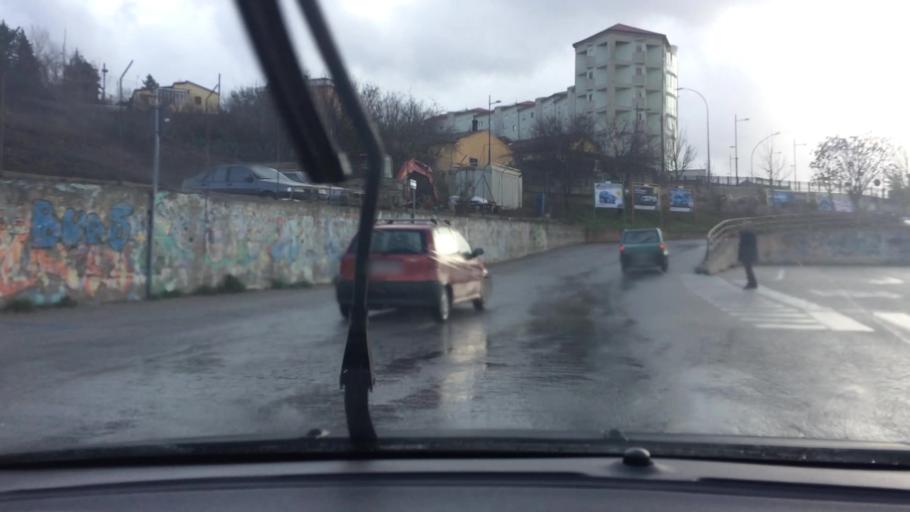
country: IT
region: Basilicate
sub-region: Provincia di Potenza
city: Potenza
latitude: 40.6396
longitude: 15.7872
